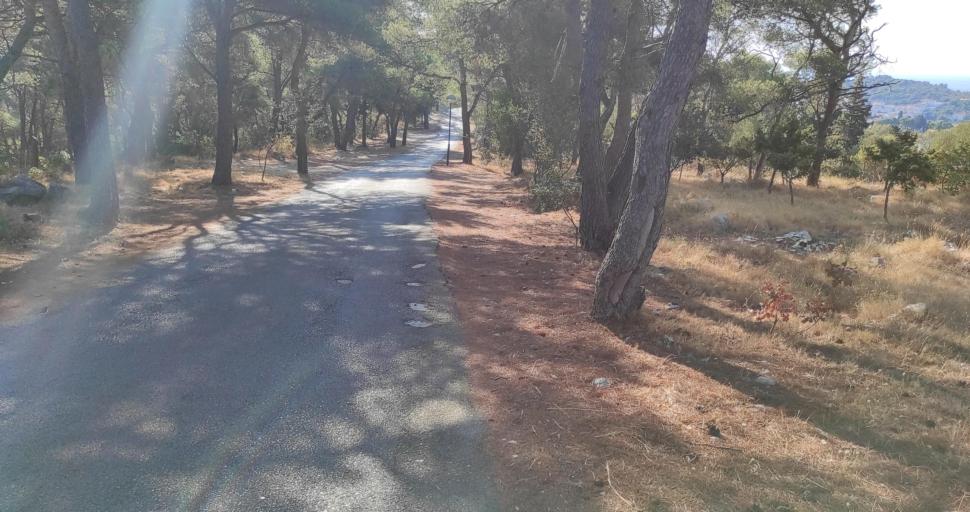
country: HR
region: Splitsko-Dalmatinska
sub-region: Grad Hvar
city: Hvar
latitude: 43.1758
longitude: 16.4392
